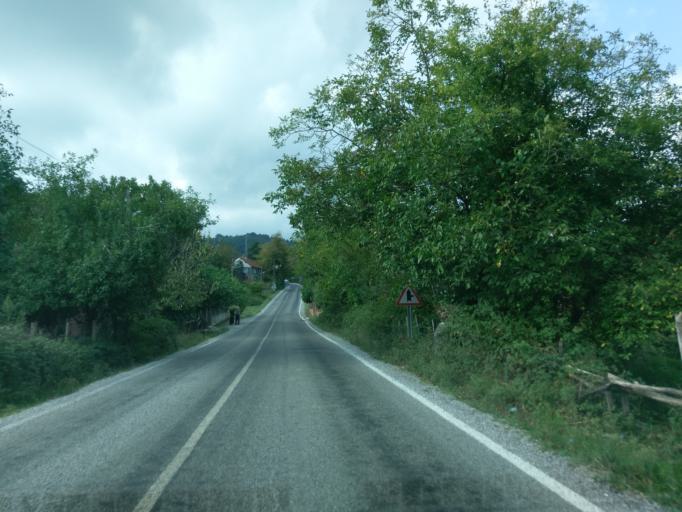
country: TR
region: Sinop
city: Helaldi
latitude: 41.9231
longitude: 34.4143
